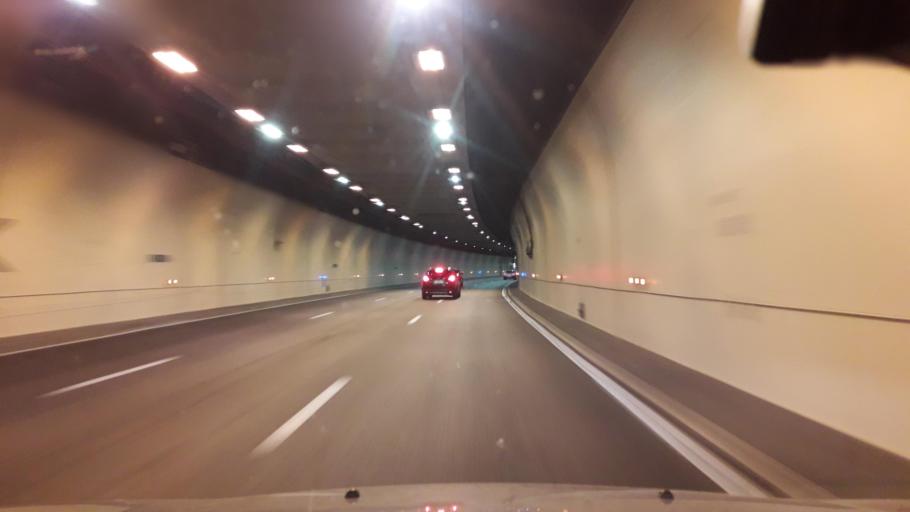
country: FR
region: Rhone-Alpes
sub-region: Departement du Rhone
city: Ecully
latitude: 45.7744
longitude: 4.7915
